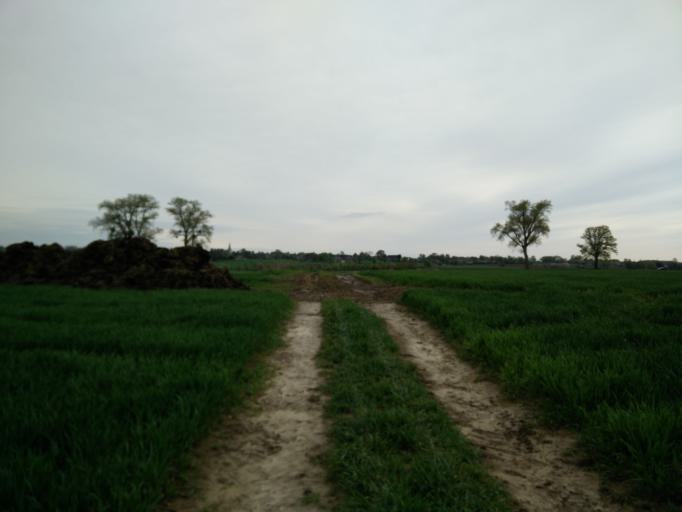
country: BE
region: Wallonia
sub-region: Province de Liege
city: Dalhem
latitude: 50.7403
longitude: 5.7464
